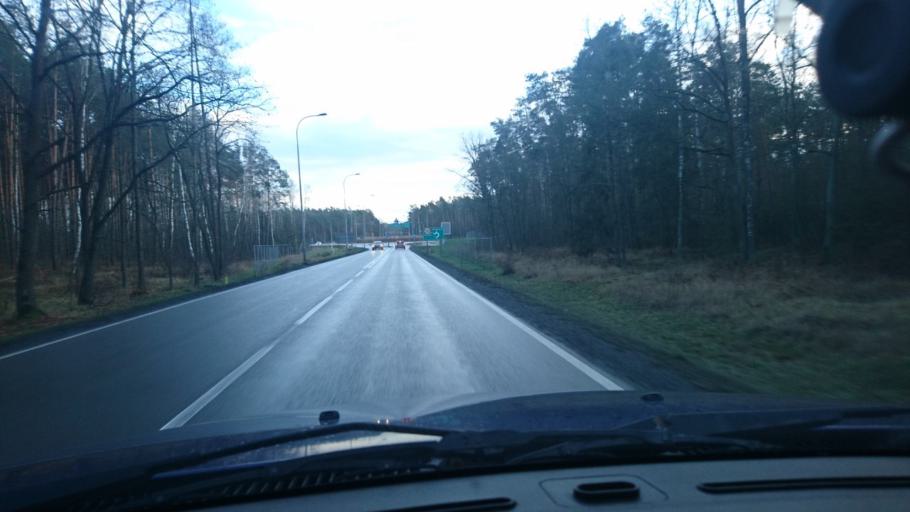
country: PL
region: Greater Poland Voivodeship
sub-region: Powiat kepinski
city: Kepno
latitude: 51.3332
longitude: 17.9570
